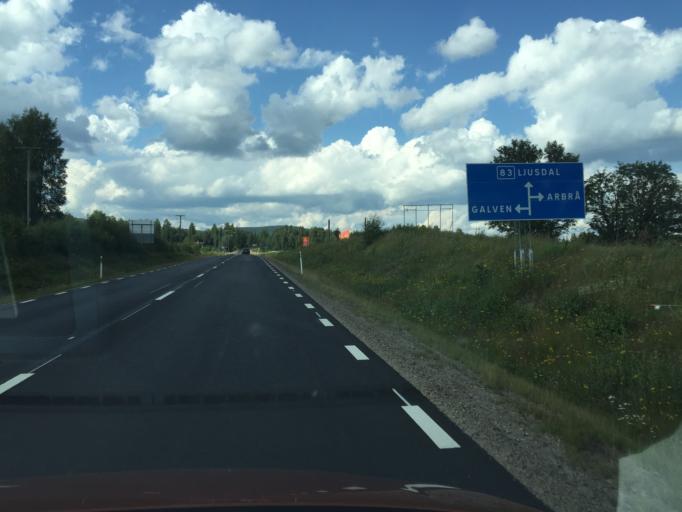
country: SE
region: Gaevleborg
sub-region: Bollnas Kommun
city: Arbra
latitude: 61.4606
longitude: 16.3720
